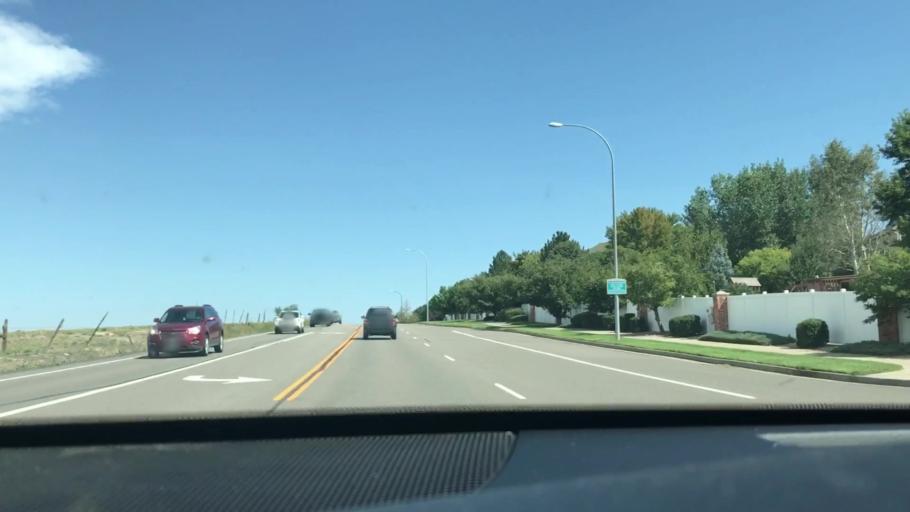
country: US
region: Colorado
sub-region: Adams County
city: Northglenn
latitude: 39.9283
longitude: -105.0045
